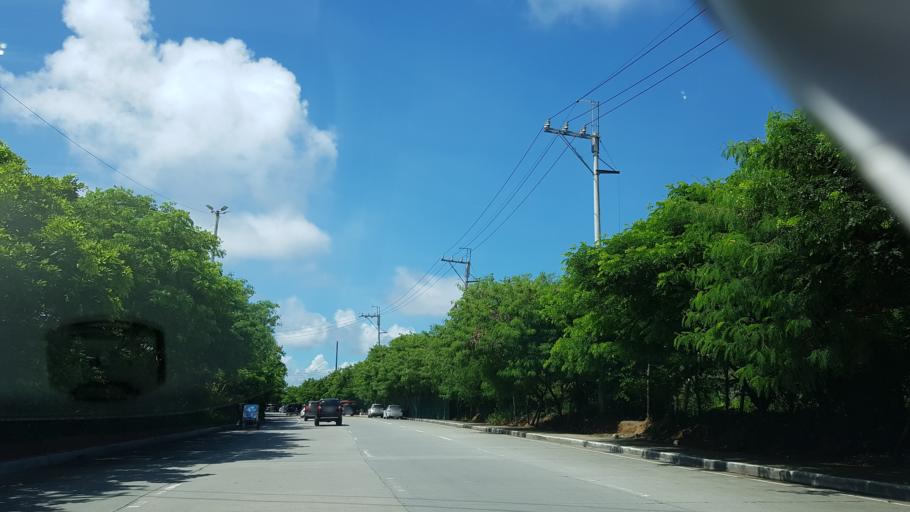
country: PH
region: Metro Manila
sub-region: City of Manila
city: Port Area
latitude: 14.5497
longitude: 120.9828
